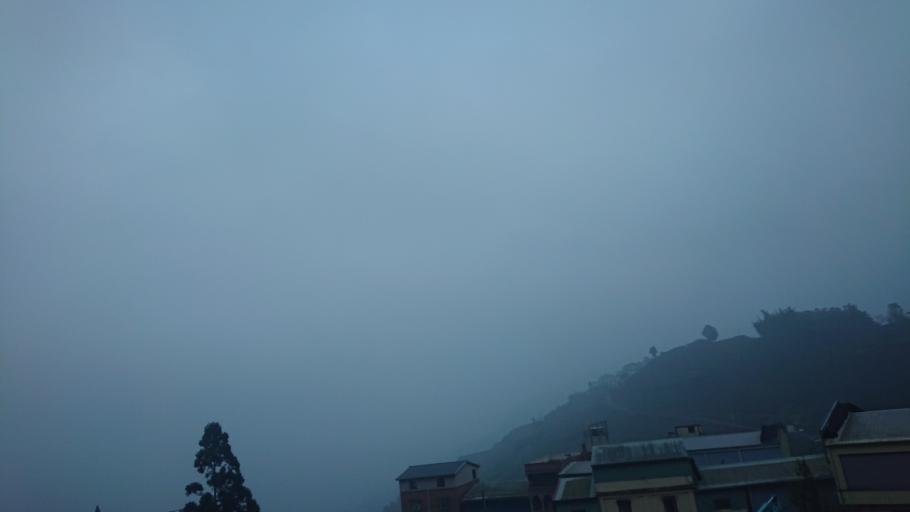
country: TW
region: Taiwan
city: Lugu
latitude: 23.5226
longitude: 120.7060
